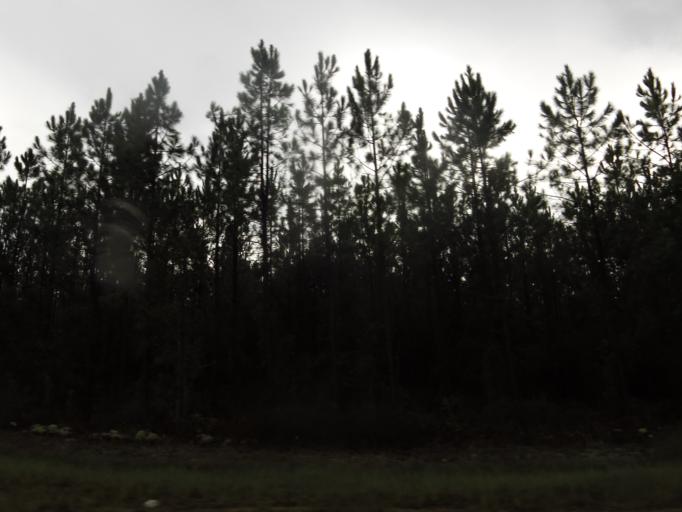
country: US
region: Georgia
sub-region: Wayne County
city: Jesup
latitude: 31.5532
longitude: -81.8892
